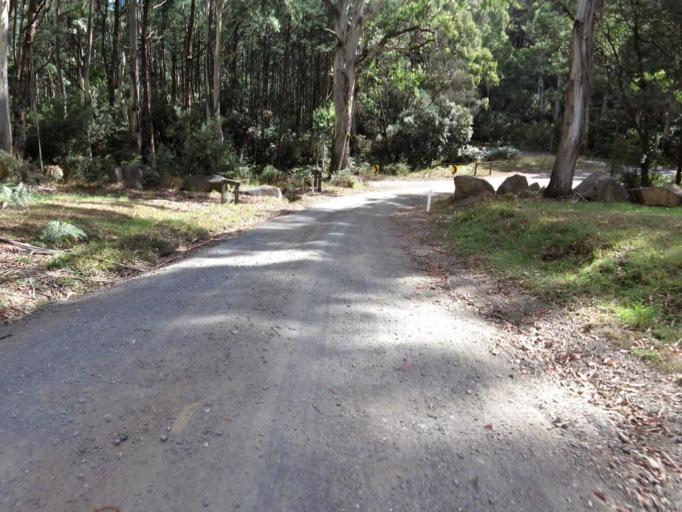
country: AU
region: Victoria
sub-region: Hume
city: Sunbury
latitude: -37.3708
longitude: 144.6008
